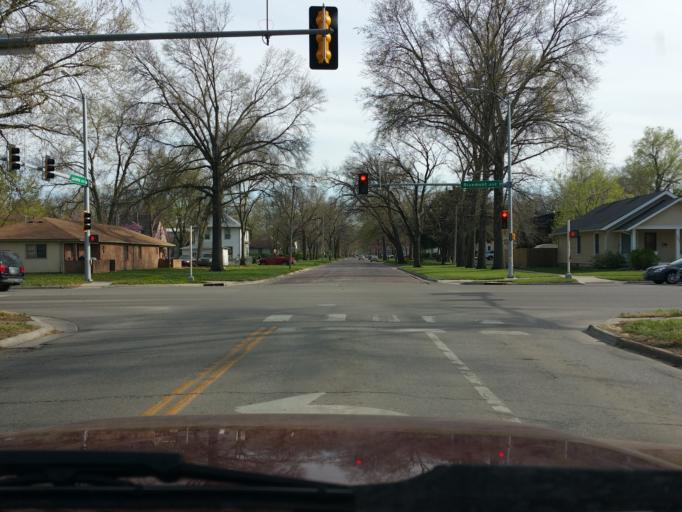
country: US
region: Kansas
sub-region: Riley County
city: Manhattan
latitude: 39.1870
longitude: -96.5667
